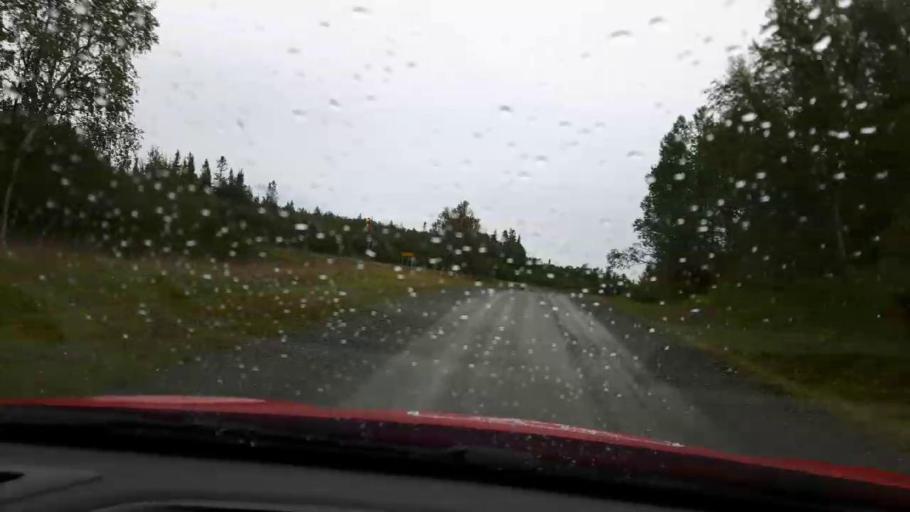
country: NO
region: Nord-Trondelag
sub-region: Meraker
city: Meraker
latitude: 63.5704
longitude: 12.2816
